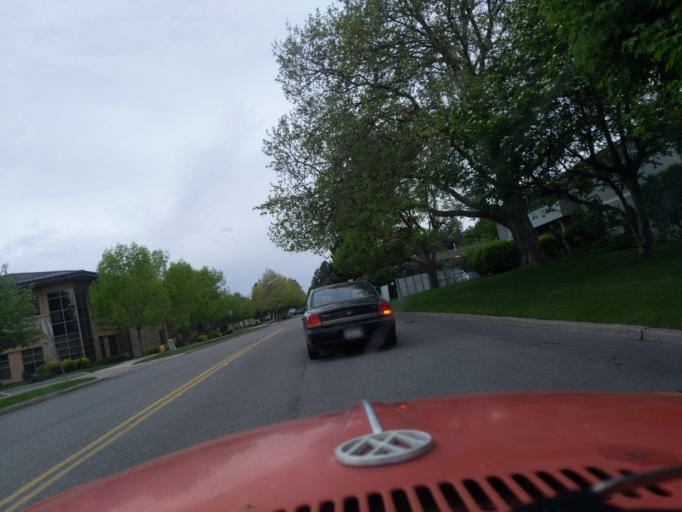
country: US
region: Washington
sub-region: Spokane County
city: Spokane
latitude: 47.6174
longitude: -117.3688
